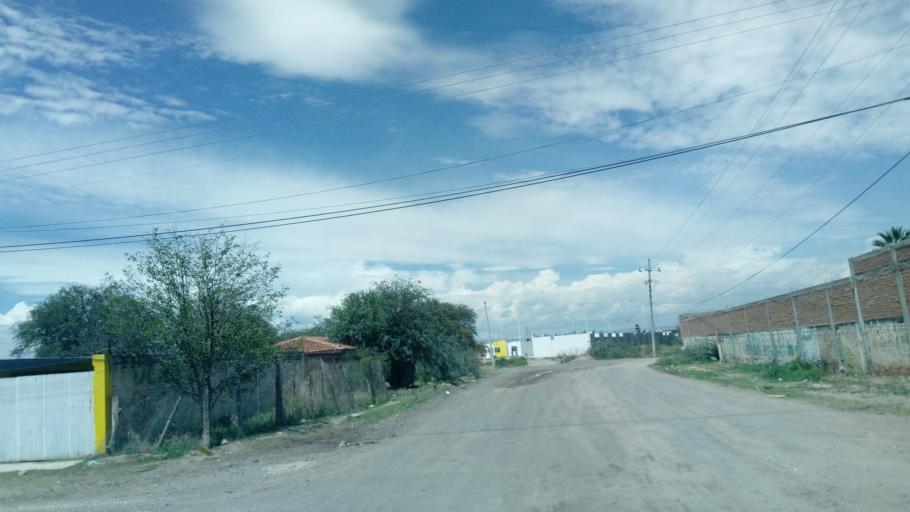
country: MX
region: Durango
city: Victoria de Durango
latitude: 24.0165
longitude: -104.5919
